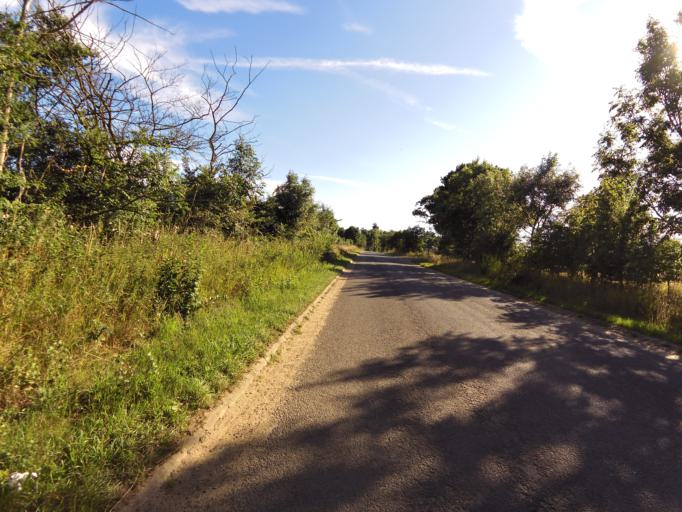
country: GB
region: England
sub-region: Suffolk
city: Kesgrave
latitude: 52.0280
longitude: 1.2585
